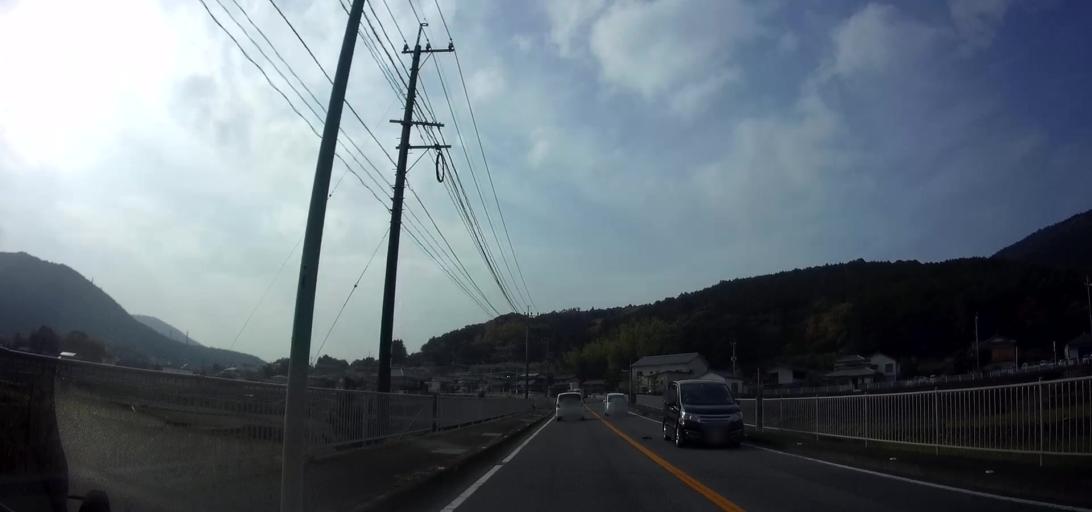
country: JP
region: Nagasaki
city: Shimabara
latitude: 32.7695
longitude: 130.2140
